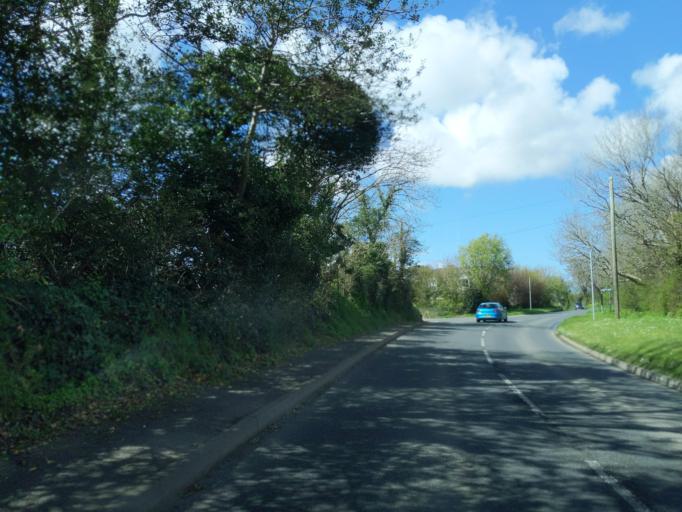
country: GB
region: England
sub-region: Cornwall
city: Wadebridge
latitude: 50.5249
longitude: -4.8309
